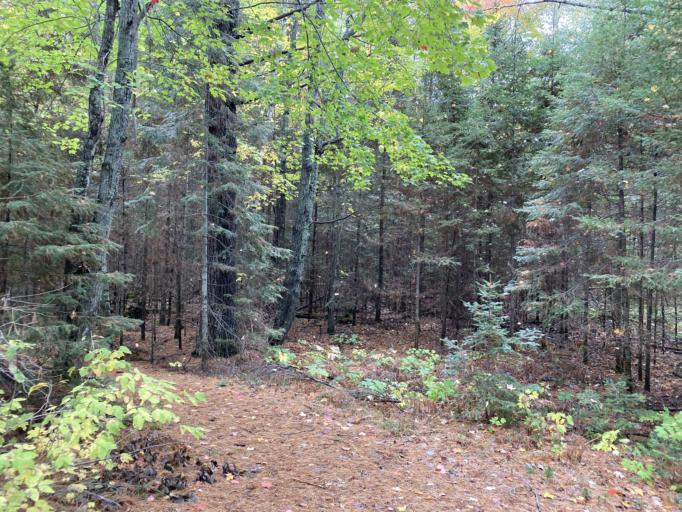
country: US
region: Michigan
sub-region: Marquette County
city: West Ishpeming
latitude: 46.5317
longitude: -88.0005
